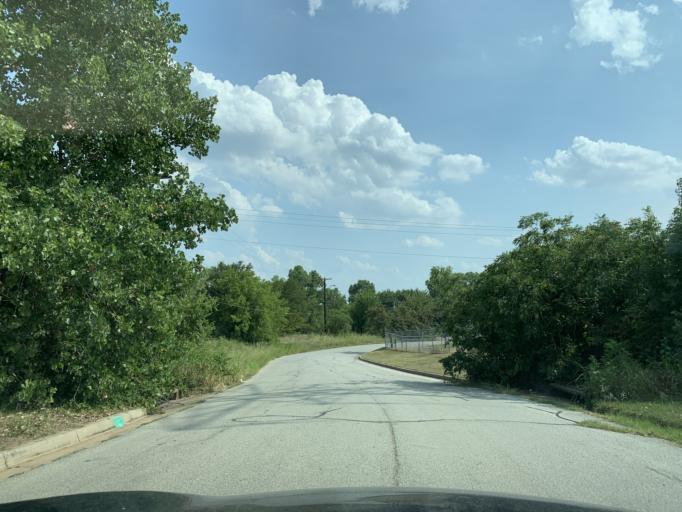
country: US
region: Texas
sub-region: Tarrant County
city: Richland Hills
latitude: 32.8081
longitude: -97.2075
